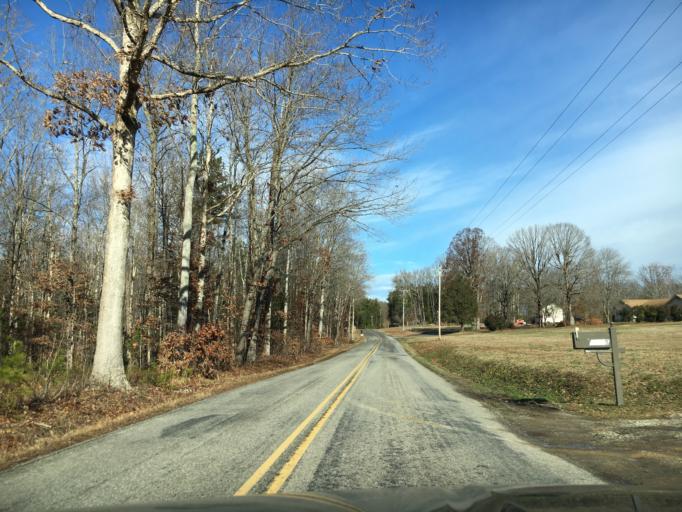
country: US
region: Virginia
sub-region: Nottoway County
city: Crewe
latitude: 37.3397
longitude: -78.1597
